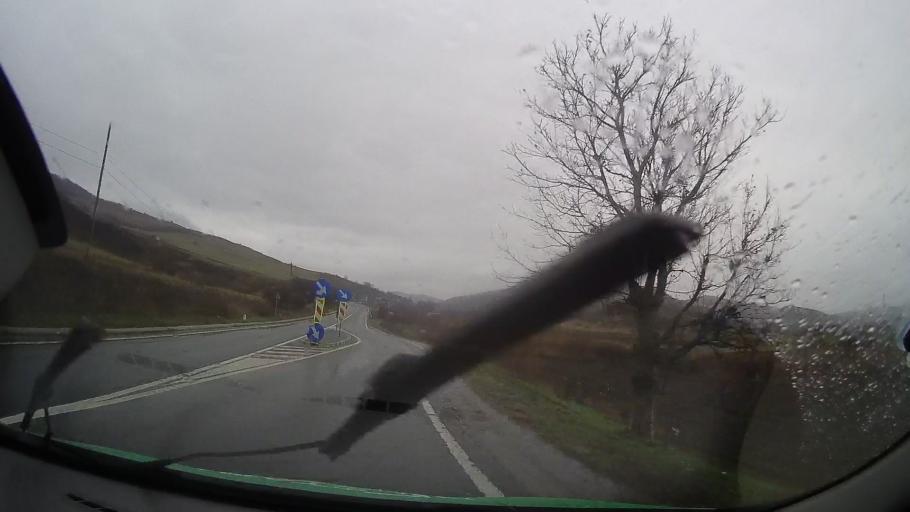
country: RO
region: Bistrita-Nasaud
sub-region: Comuna Galatii Bistritei
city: Galatii Bistritei
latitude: 46.9541
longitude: 24.4452
